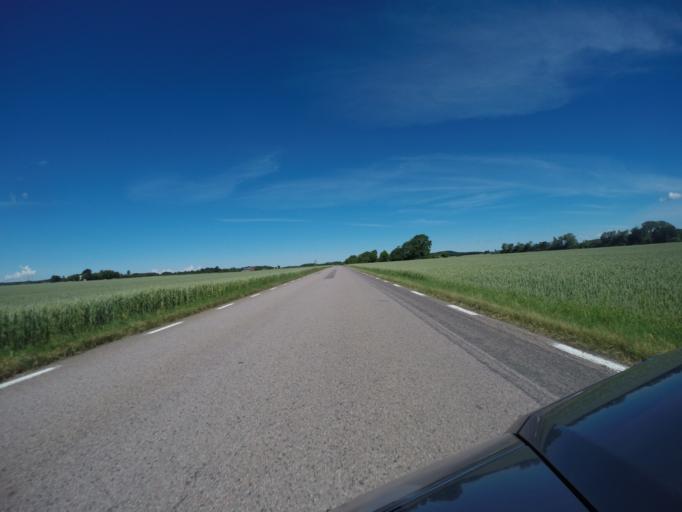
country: SE
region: Skane
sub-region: Helsingborg
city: Odakra
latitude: 56.1381
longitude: 12.7363
